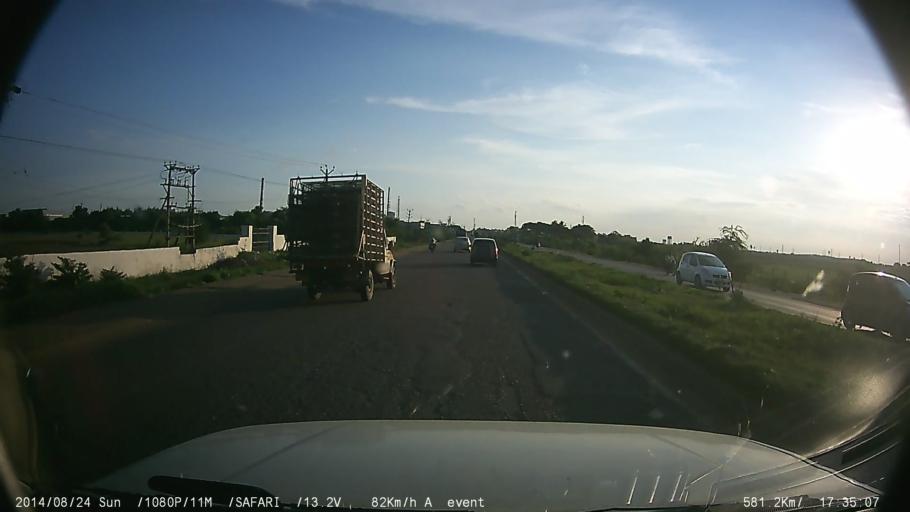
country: IN
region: Tamil Nadu
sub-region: Kancheepuram
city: Sriperumbudur
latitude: 12.9446
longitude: 79.9218
